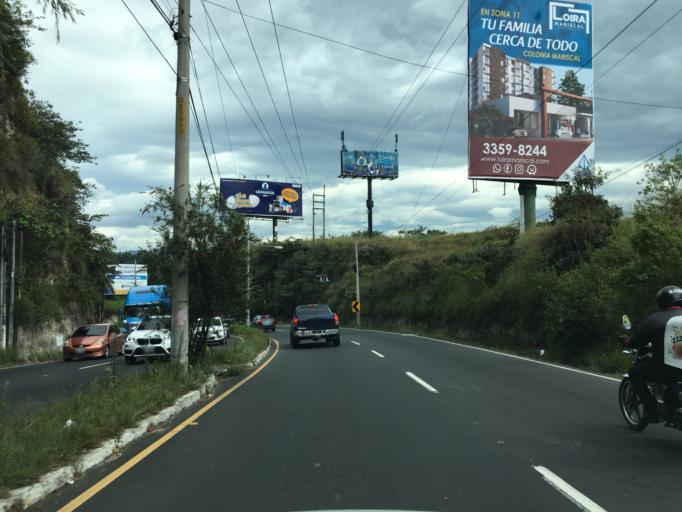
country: GT
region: Guatemala
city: Mixco
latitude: 14.5903
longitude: -90.5760
